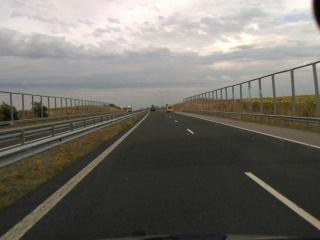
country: BG
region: Sliven
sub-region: Obshtina Sliven
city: Kermen
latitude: 42.5117
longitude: 26.3625
